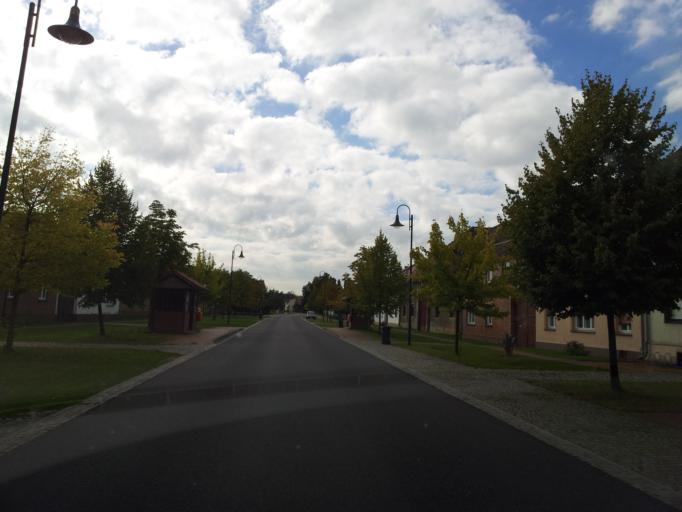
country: DE
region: Brandenburg
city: Sallgast
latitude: 51.5978
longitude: 13.7786
